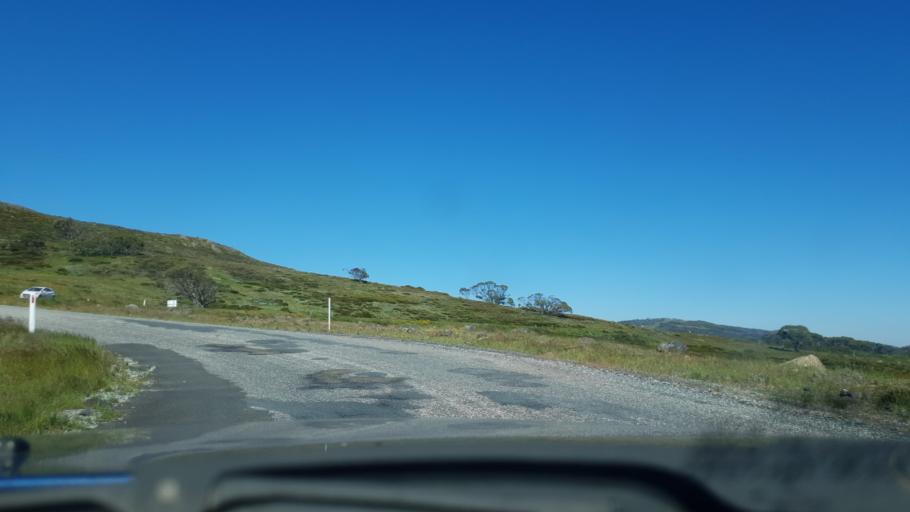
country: AU
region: Victoria
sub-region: Alpine
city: Mount Beauty
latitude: -36.8844
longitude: 147.3174
